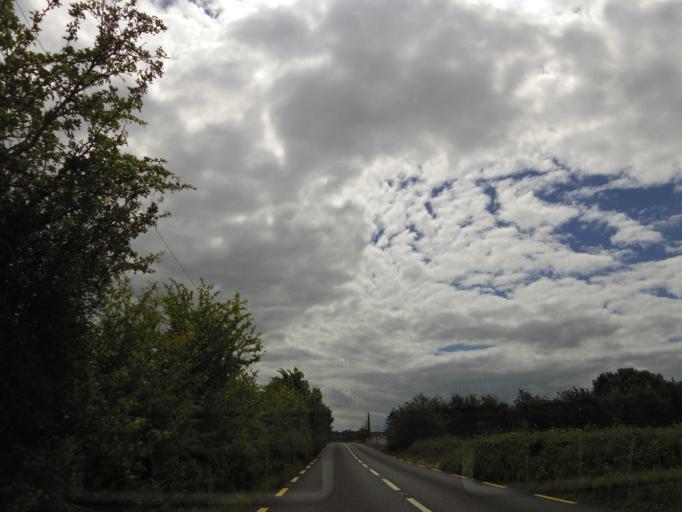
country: IE
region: Munster
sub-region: North Tipperary
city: Nenagh
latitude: 52.7862
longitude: -8.0350
